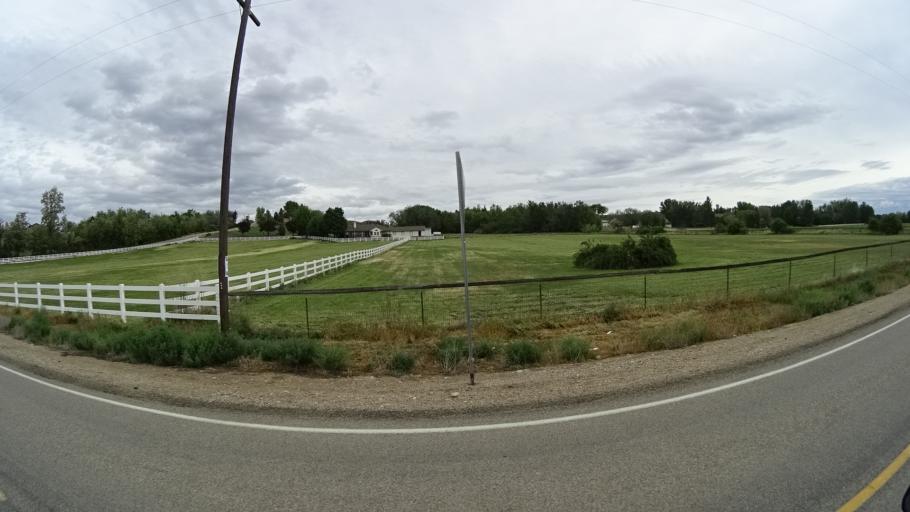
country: US
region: Idaho
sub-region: Ada County
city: Star
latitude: 43.7175
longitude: -116.5111
